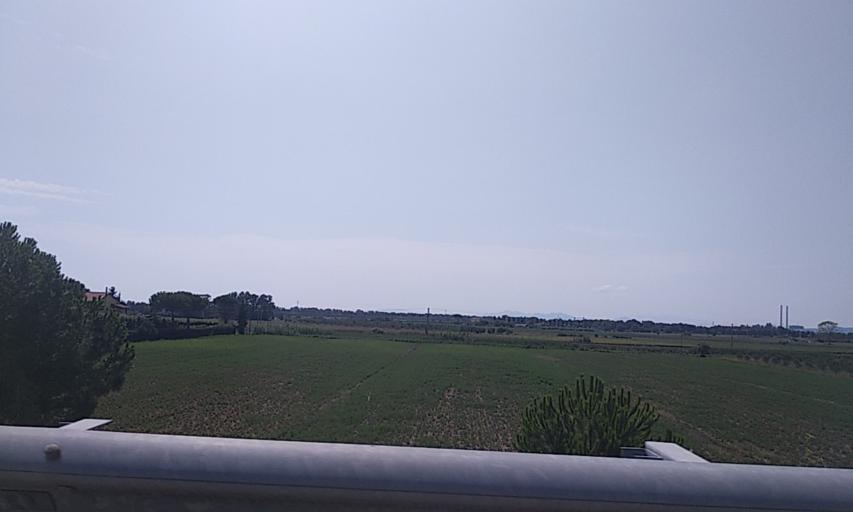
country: IT
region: Tuscany
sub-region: Provincia di Livorno
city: Riotorto
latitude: 42.9724
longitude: 10.6633
